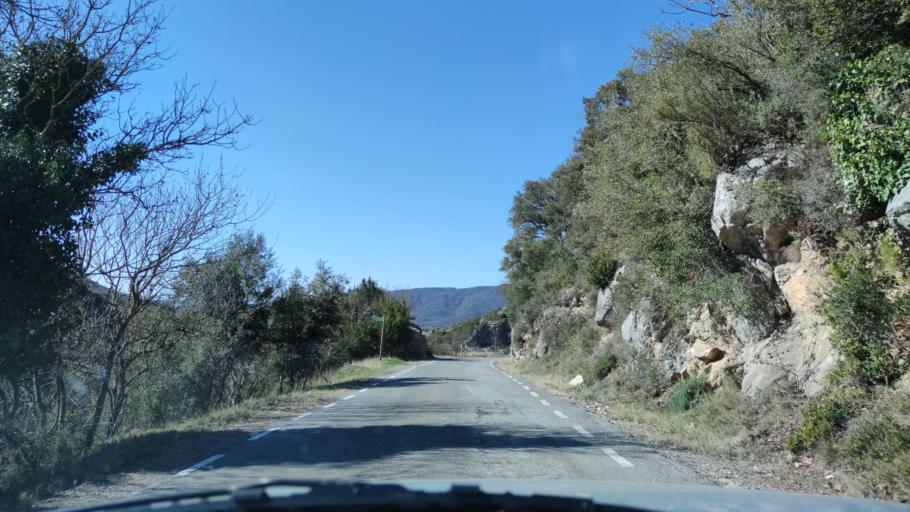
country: ES
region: Catalonia
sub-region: Provincia de Lleida
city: Artesa de Segre
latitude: 42.0060
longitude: 1.0309
